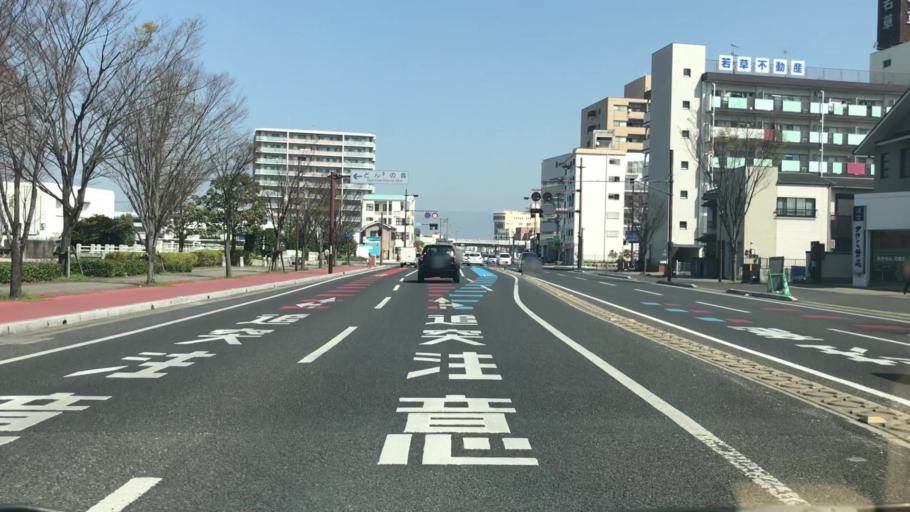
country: JP
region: Saga Prefecture
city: Saga-shi
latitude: 33.2604
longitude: 130.2932
